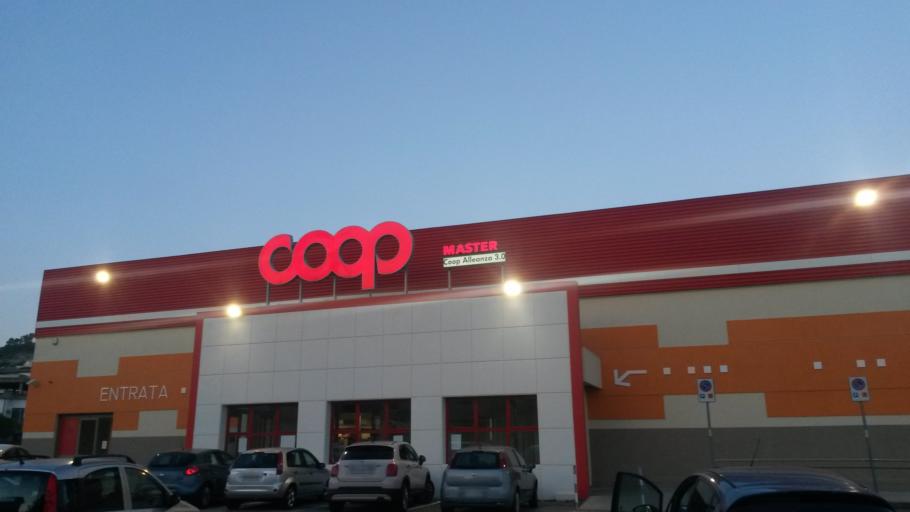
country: IT
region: Calabria
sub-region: Provincia di Catanzaro
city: Catanzaro
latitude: 38.8874
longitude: 16.6028
